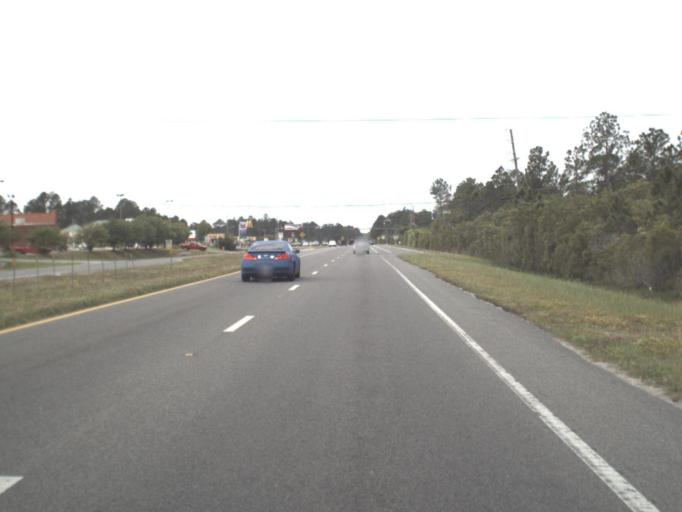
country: US
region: Florida
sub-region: Escambia County
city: Myrtle Grove
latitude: 30.4034
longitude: -87.3386
